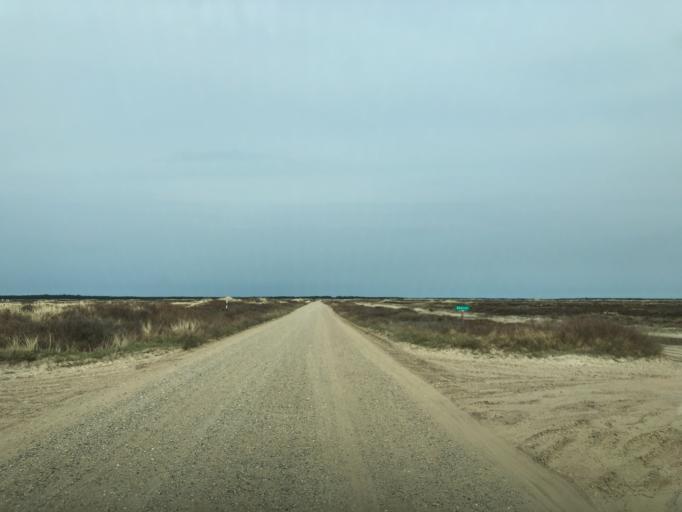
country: DK
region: South Denmark
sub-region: Varde Kommune
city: Oksbol
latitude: 55.5741
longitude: 8.1397
